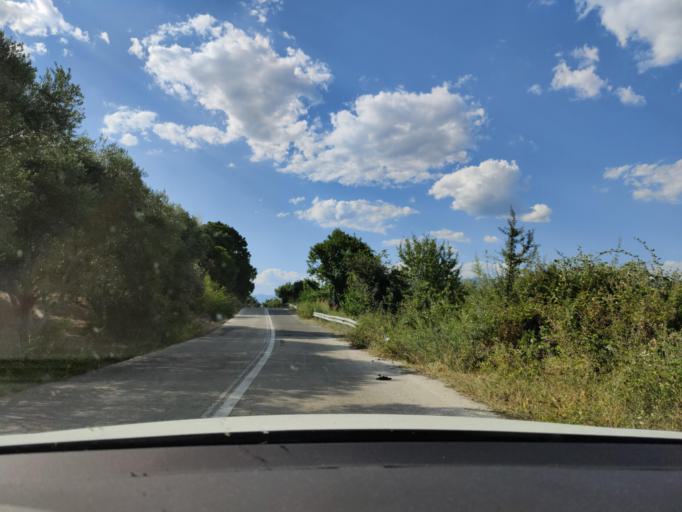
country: GR
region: Central Macedonia
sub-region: Nomos Serron
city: Chrysochorafa
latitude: 41.1680
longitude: 23.1791
